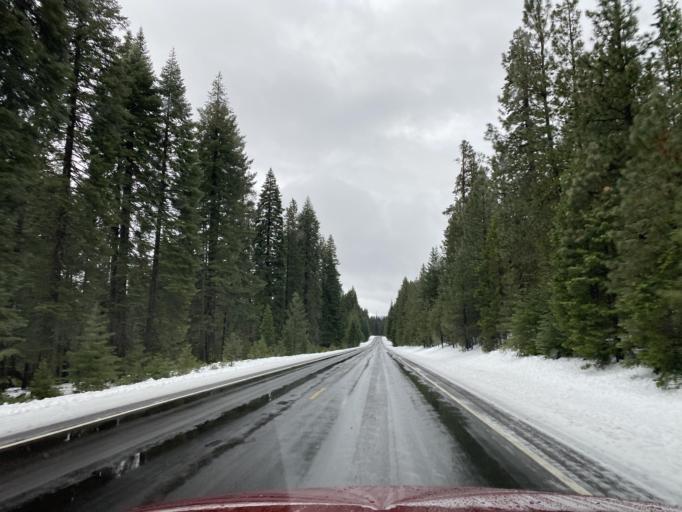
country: US
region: Oregon
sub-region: Klamath County
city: Klamath Falls
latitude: 42.5106
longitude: -122.0833
